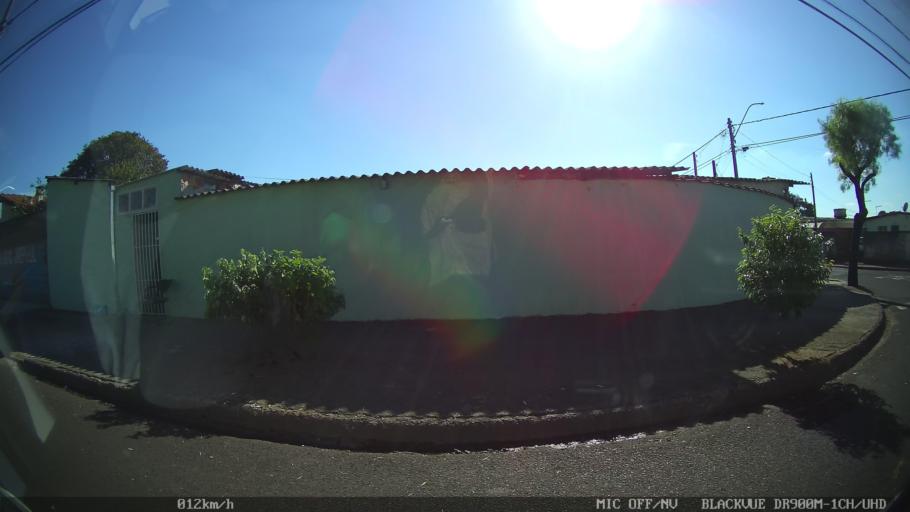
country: BR
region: Sao Paulo
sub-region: Franca
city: Franca
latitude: -20.4976
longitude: -47.4157
